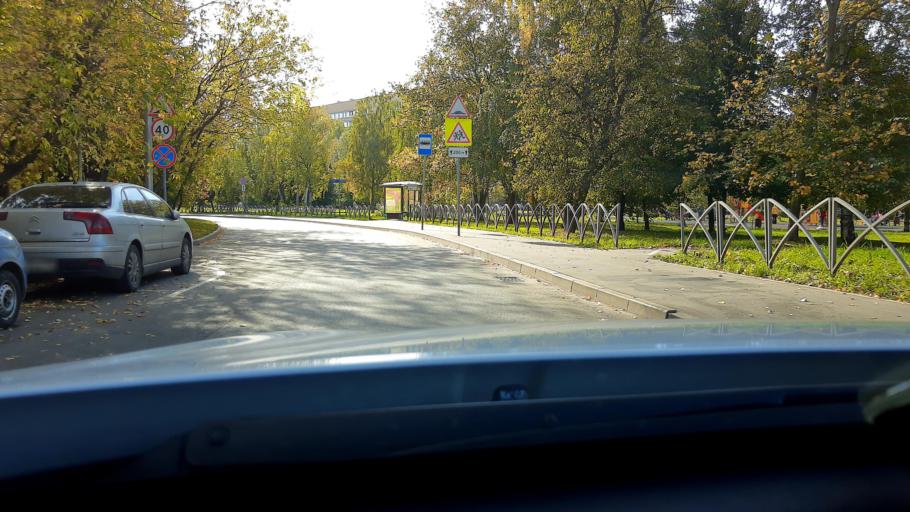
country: RU
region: Moscow
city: Vagonoremont
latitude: 55.8967
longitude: 37.5371
